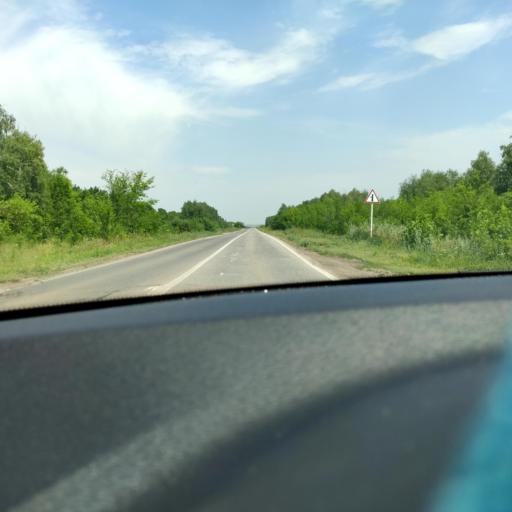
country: RU
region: Samara
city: Petra-Dubrava
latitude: 53.3416
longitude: 50.4652
